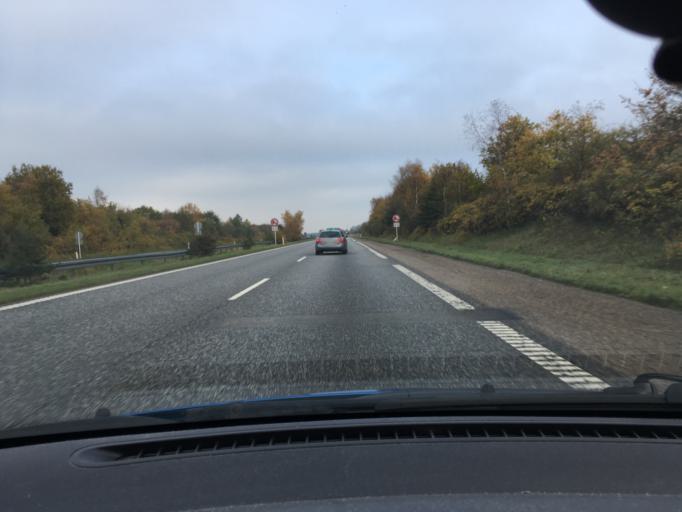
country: DK
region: South Denmark
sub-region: Aabenraa Kommune
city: Krusa
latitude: 54.9154
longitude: 9.3824
